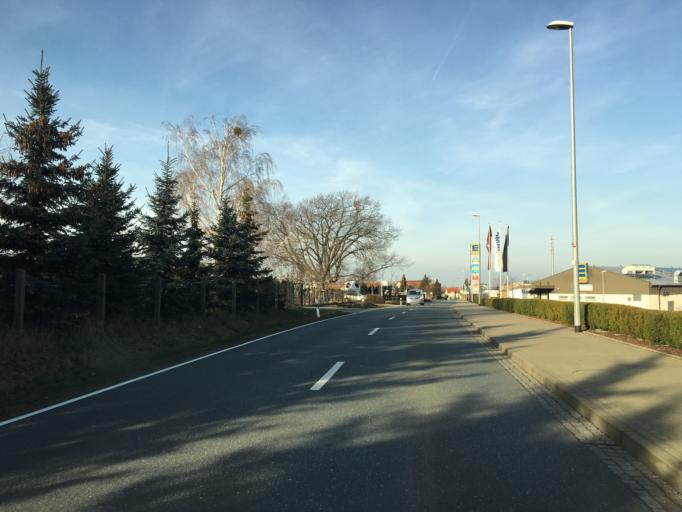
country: DE
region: Saxony
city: Oschatz
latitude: 51.2896
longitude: 13.1239
